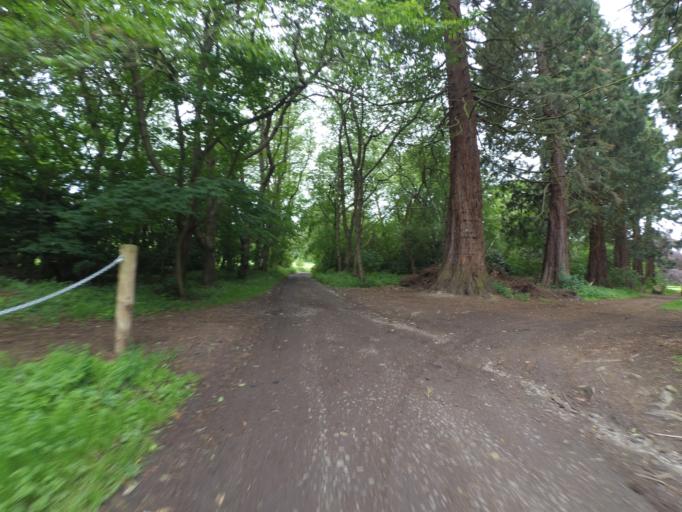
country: GB
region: Scotland
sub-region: East Lothian
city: Musselburgh
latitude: 55.9161
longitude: -3.0175
